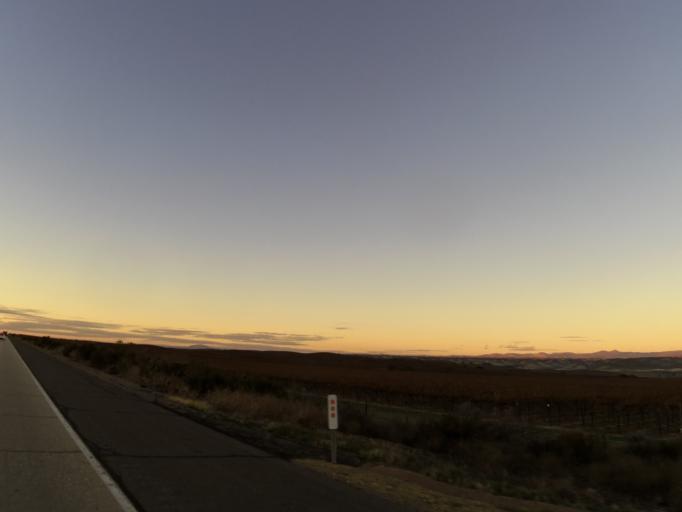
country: US
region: California
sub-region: Monterey County
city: King City
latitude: 36.0414
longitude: -120.9549
